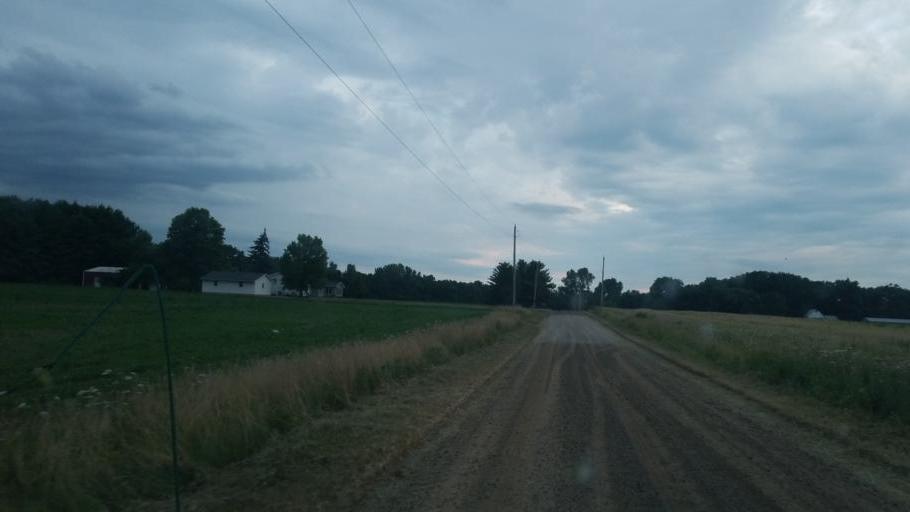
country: US
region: Ohio
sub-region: Defiance County
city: Hicksville
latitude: 41.3283
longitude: -84.8490
